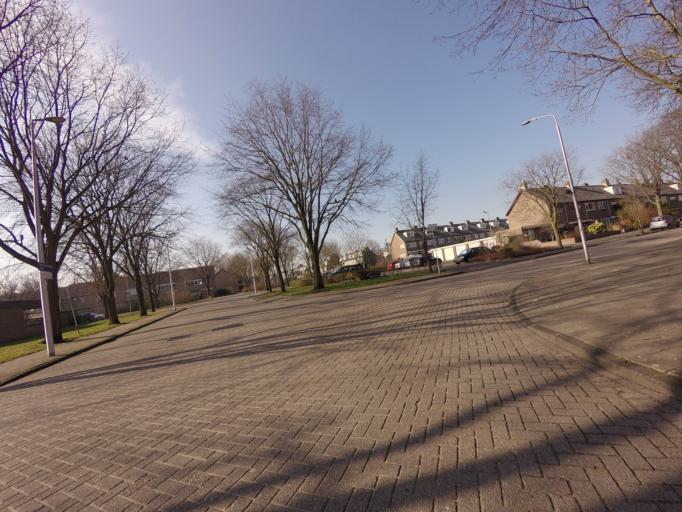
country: NL
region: North Holland
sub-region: Gemeente Zandvoort
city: Zandvoort
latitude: 52.3782
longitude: 4.5553
